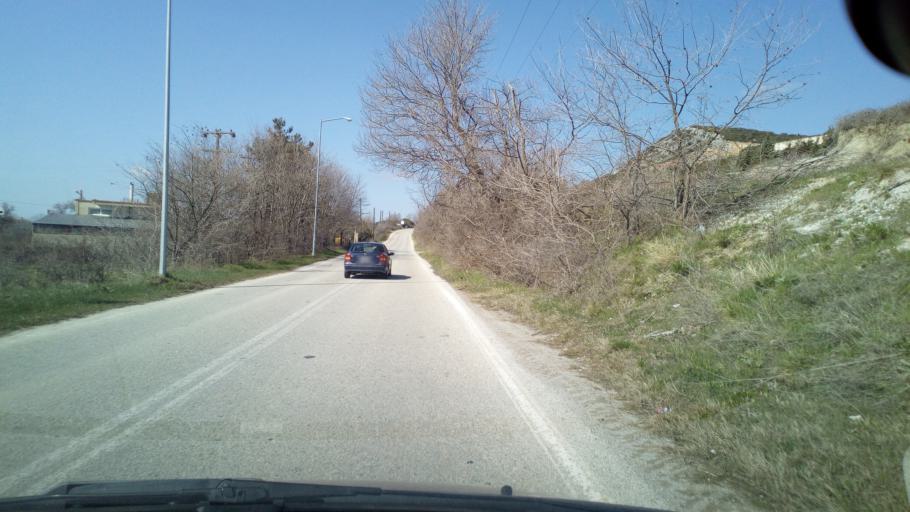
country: GR
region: Central Macedonia
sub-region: Nomos Thessalonikis
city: Chortiatis
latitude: 40.6254
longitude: 23.0811
